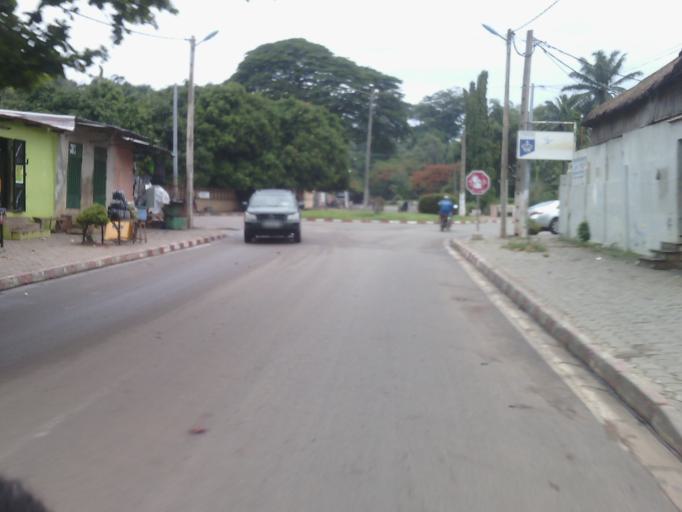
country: BJ
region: Queme
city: Porto-Novo
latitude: 6.4733
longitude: 2.6178
